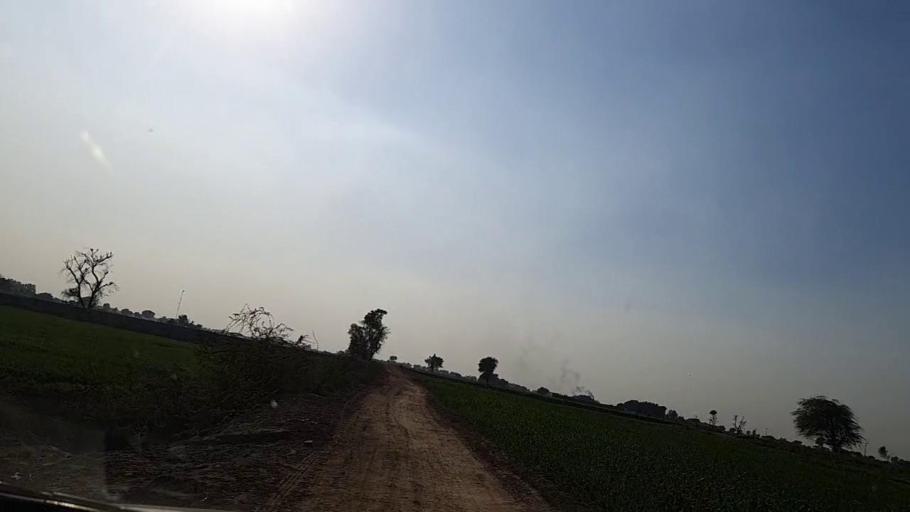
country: PK
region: Sindh
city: Sakrand
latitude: 26.1227
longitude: 68.2463
